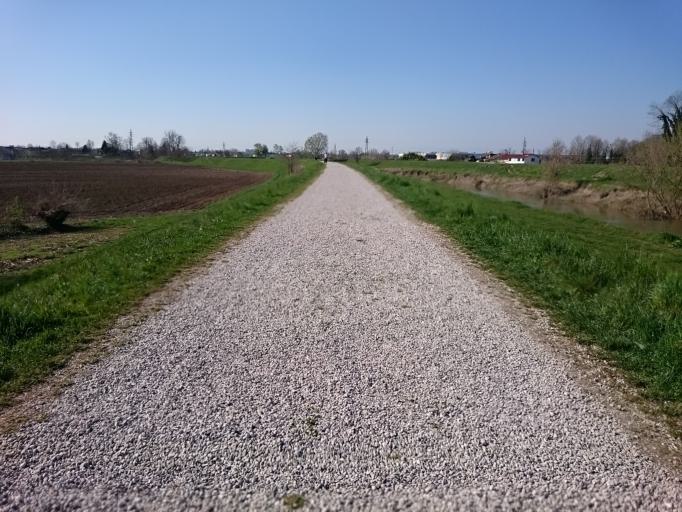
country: IT
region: Veneto
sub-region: Provincia di Padova
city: Ponte San Nicolo
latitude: 45.3752
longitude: 11.9296
